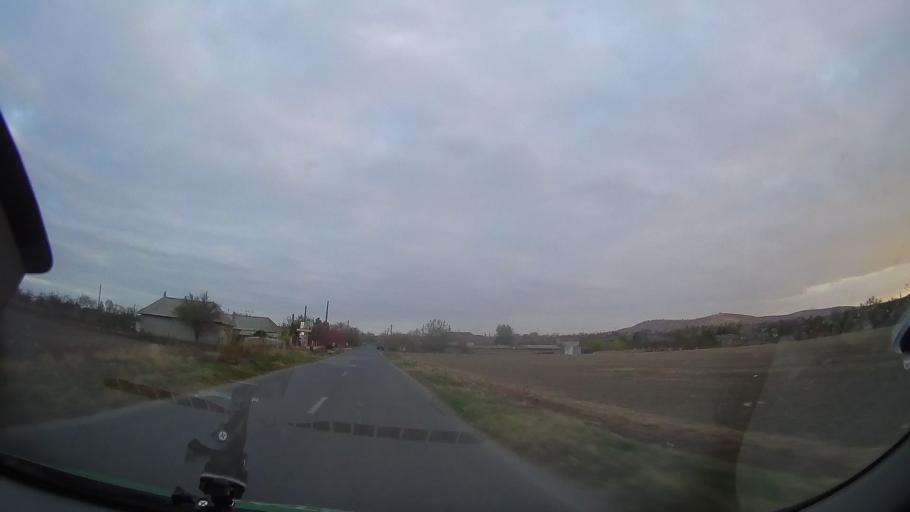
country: RO
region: Tulcea
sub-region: Comuna Mihai Bravu
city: Turda
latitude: 44.9819
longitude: 28.6148
